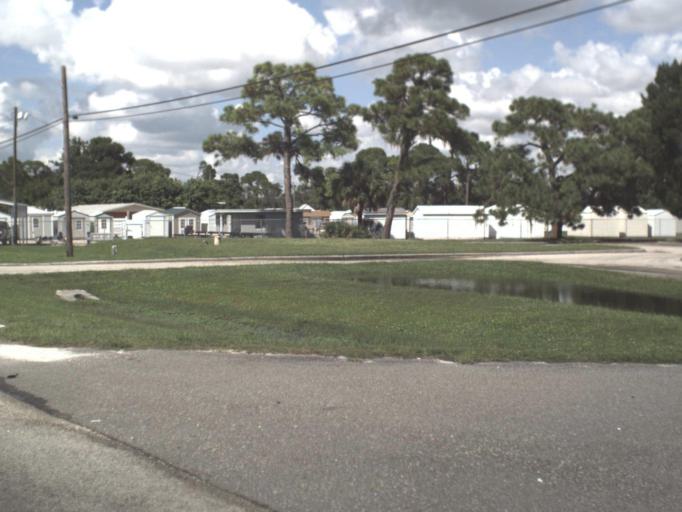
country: US
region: Florida
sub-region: Sarasota County
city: Osprey
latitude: 27.1845
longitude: -82.4845
